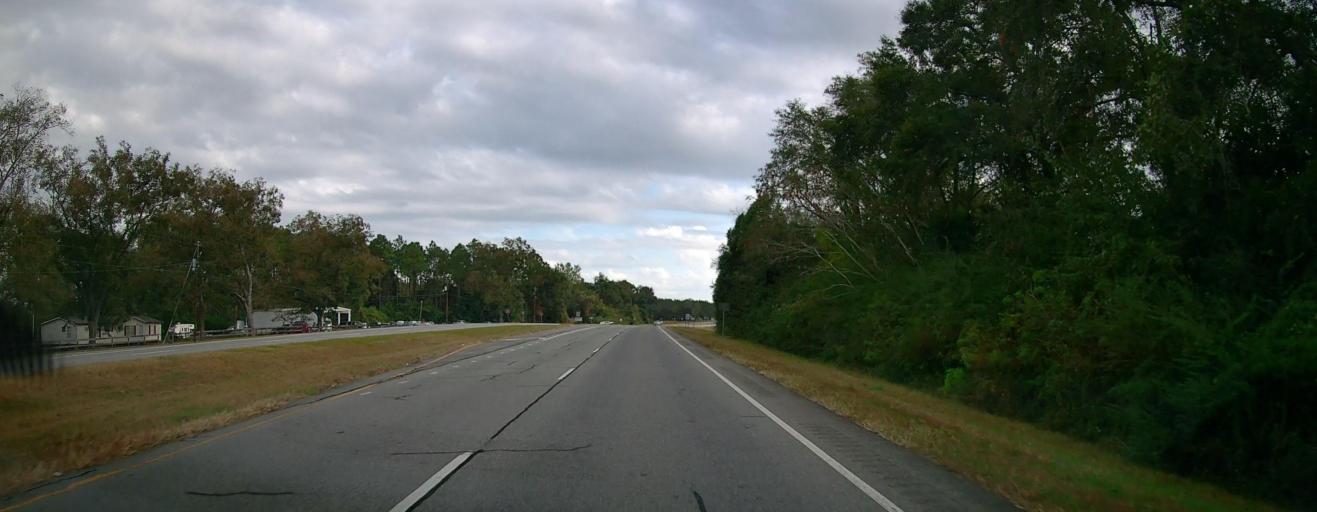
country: US
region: Georgia
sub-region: Thomas County
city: Meigs
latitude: 31.0798
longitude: -84.0822
